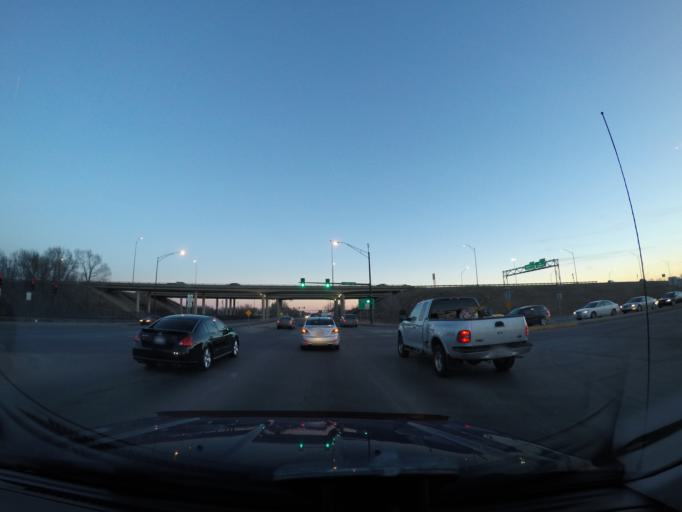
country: US
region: Kansas
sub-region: Sedgwick County
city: Wichita
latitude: 37.7145
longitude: -97.4004
